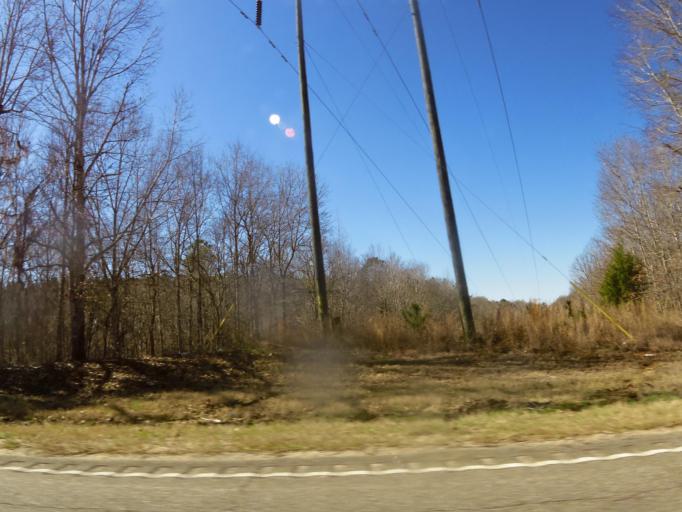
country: US
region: Alabama
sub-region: Bullock County
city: Union Springs
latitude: 32.1353
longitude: -85.7670
